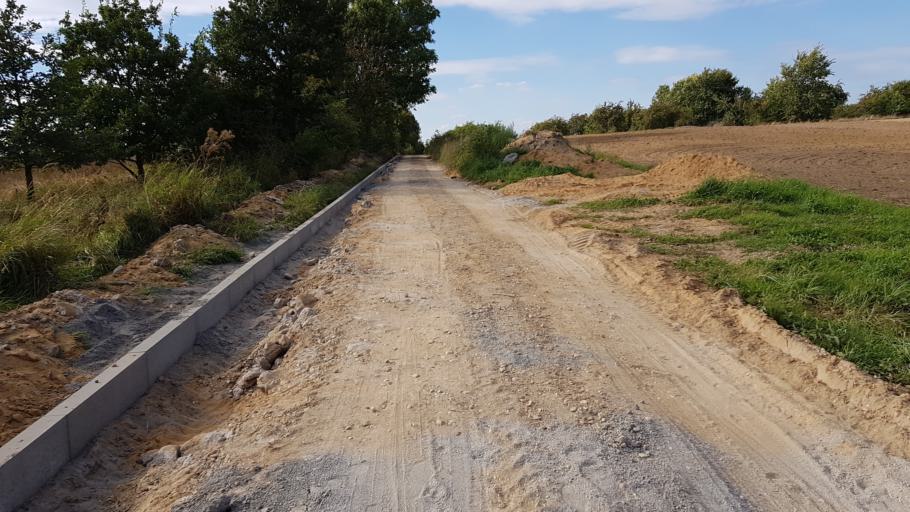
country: PL
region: West Pomeranian Voivodeship
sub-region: Powiat policki
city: Kolbaskowo
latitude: 53.3750
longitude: 14.4309
